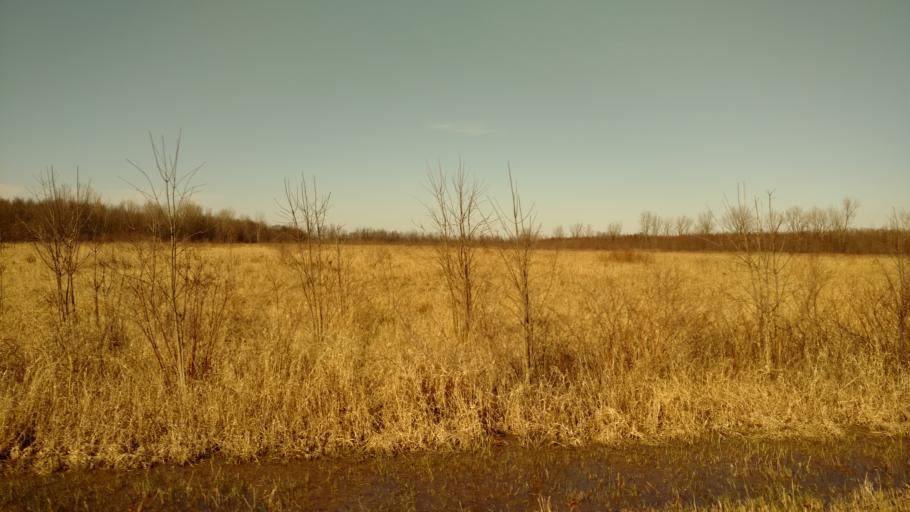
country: US
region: Ohio
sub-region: Wyandot County
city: Upper Sandusky
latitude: 40.6945
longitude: -83.3317
